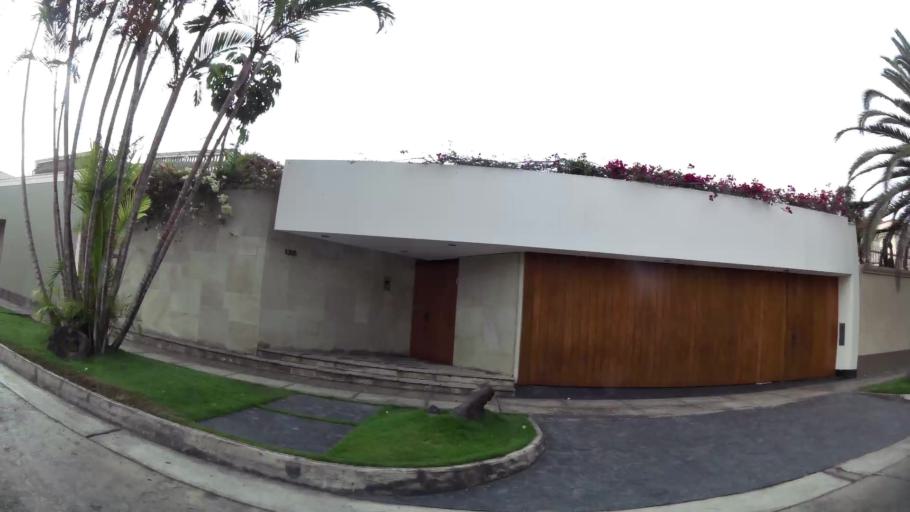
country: PE
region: Lima
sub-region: Lima
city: San Isidro
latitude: -12.0999
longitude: -77.0542
